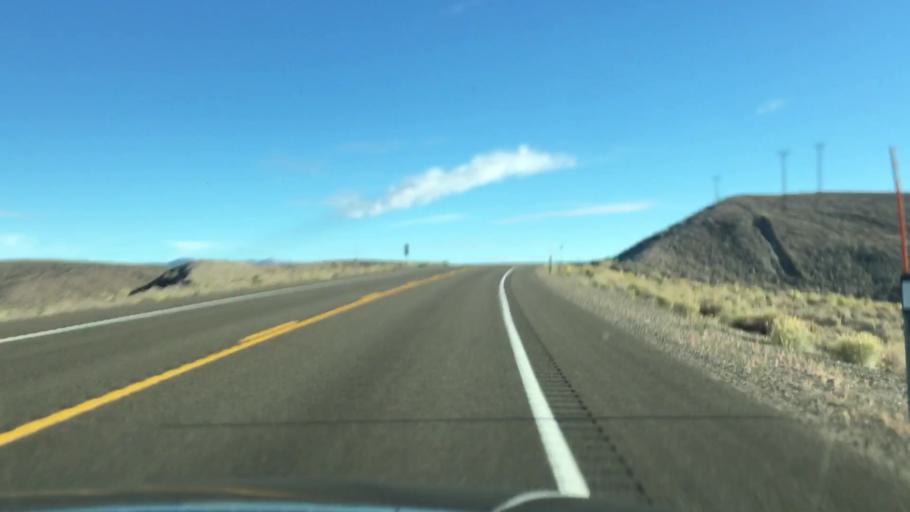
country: US
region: Nevada
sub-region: Mineral County
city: Hawthorne
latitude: 38.2188
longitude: -118.0069
